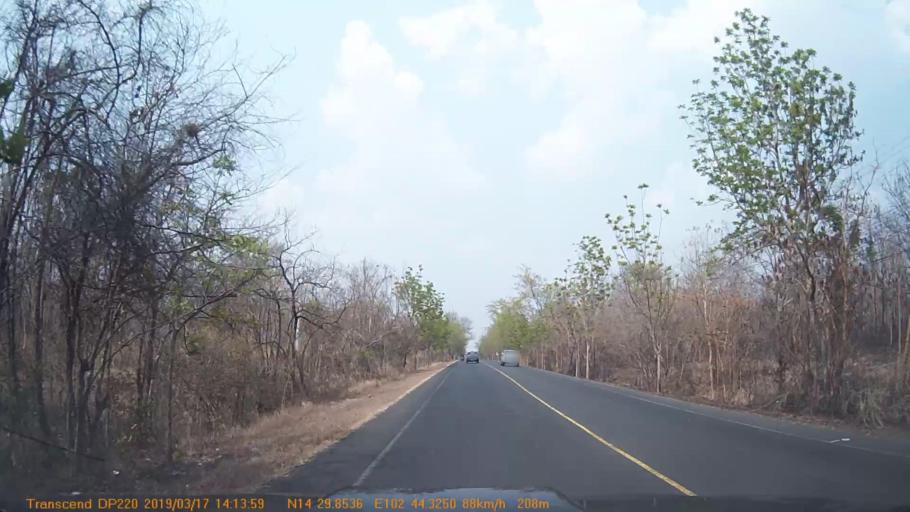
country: TH
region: Buriram
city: Pa Kham
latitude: 14.4977
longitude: 102.7388
